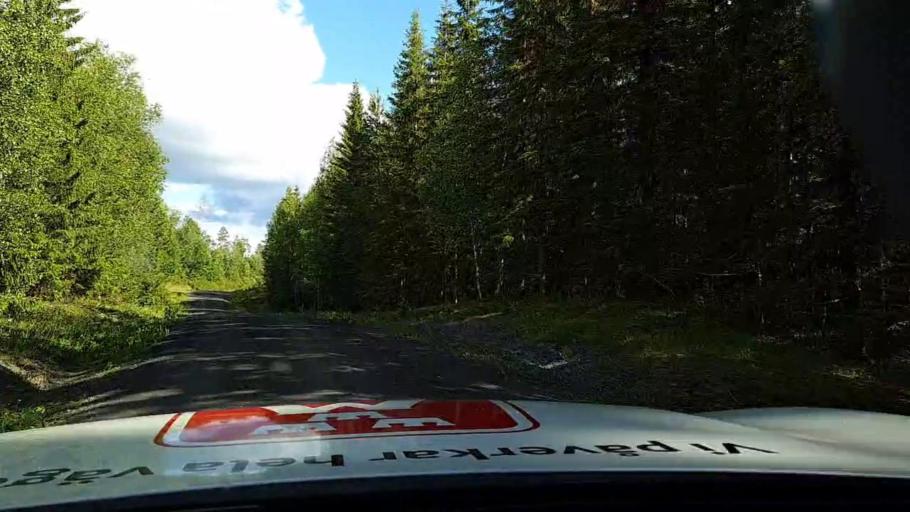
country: SE
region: Jaemtland
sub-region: Krokoms Kommun
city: Valla
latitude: 63.3217
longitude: 13.7558
